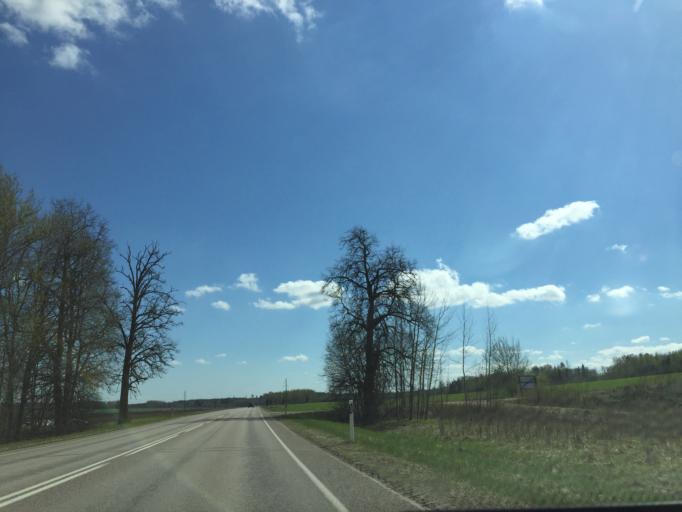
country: EE
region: Valgamaa
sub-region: Valga linn
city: Valga
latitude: 57.8843
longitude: 26.0588
